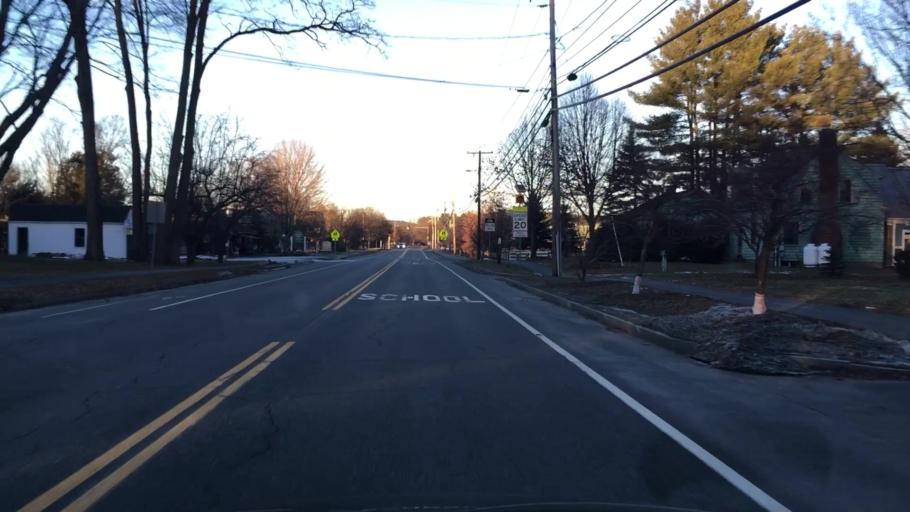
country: US
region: New Hampshire
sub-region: Grafton County
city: Hanover
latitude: 43.7211
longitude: -72.2720
